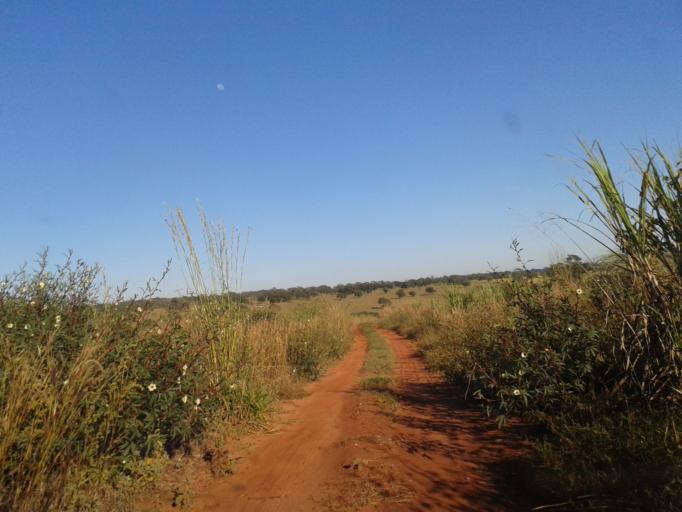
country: BR
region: Minas Gerais
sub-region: Santa Vitoria
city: Santa Vitoria
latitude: -19.0198
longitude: -50.3763
